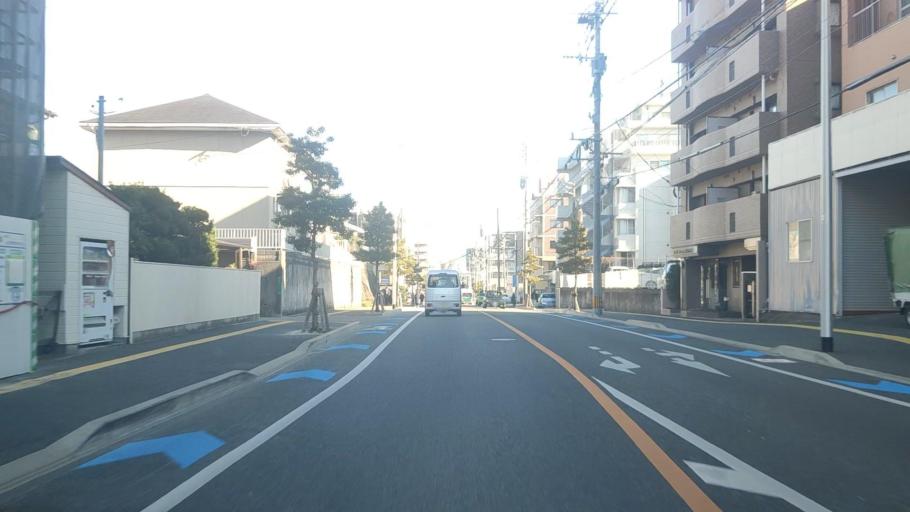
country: JP
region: Fukuoka
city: Fukuoka-shi
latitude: 33.5537
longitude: 130.3544
